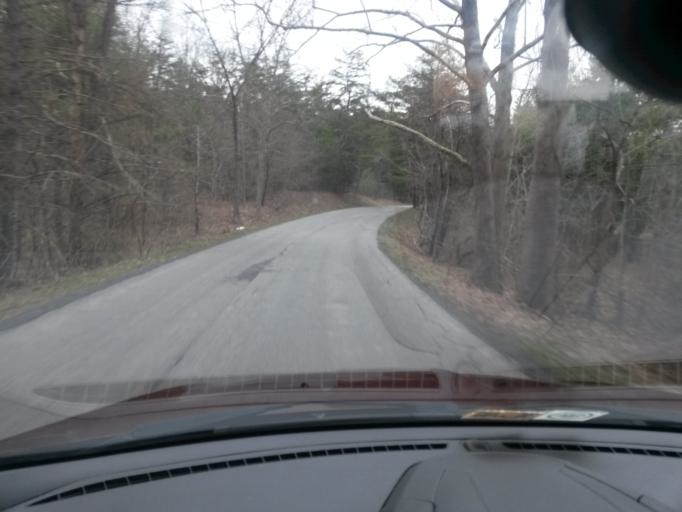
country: US
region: Virginia
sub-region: Bath County
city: Warm Springs
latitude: 38.0294
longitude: -79.8589
